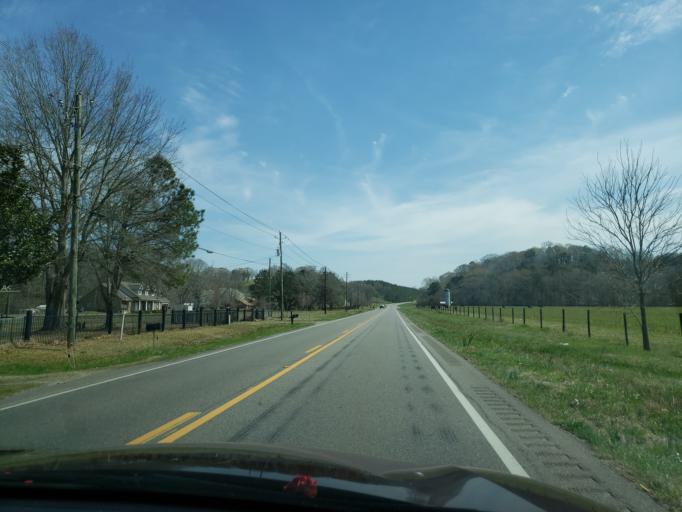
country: US
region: Alabama
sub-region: Autauga County
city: Prattville
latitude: 32.4328
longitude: -86.5705
